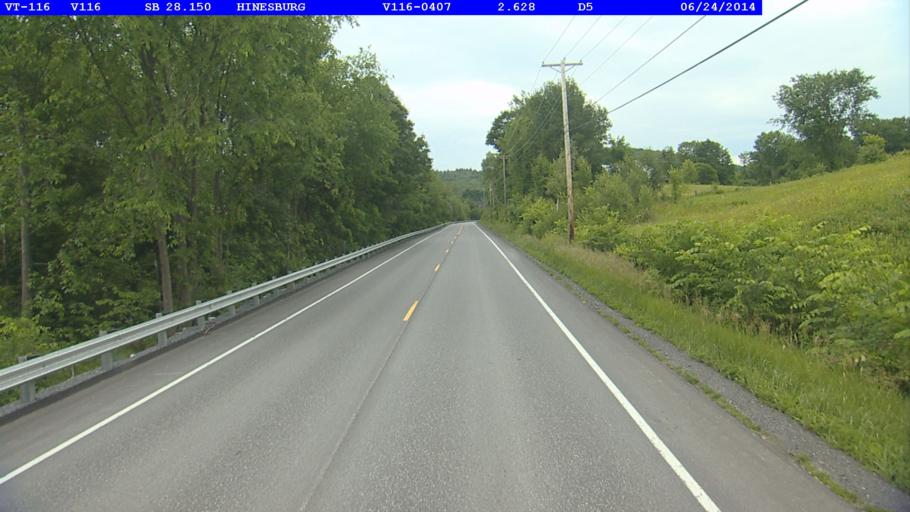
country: US
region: Vermont
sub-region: Chittenden County
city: Hinesburg
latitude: 44.3142
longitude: -73.0821
